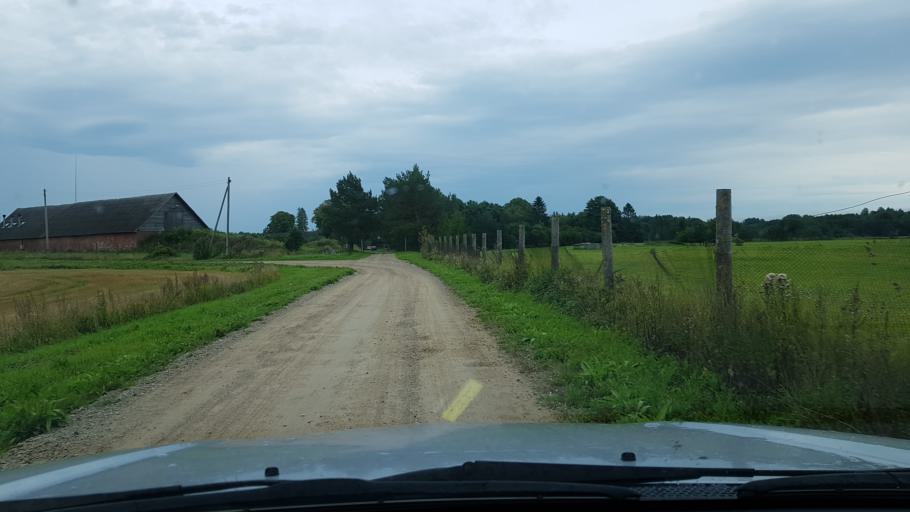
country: EE
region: Harju
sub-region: Rae vald
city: Jueri
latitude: 59.3386
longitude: 24.9412
